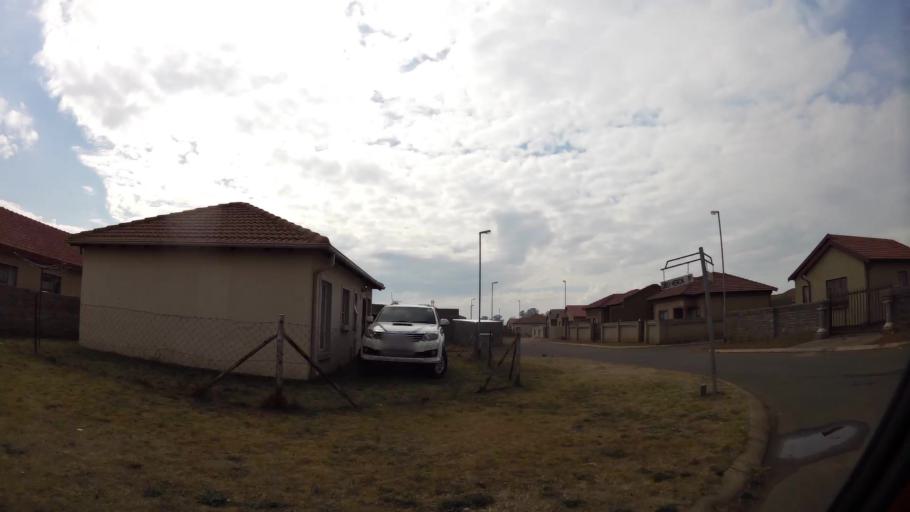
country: ZA
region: Gauteng
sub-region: Sedibeng District Municipality
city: Vanderbijlpark
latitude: -26.6832
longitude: 27.8498
